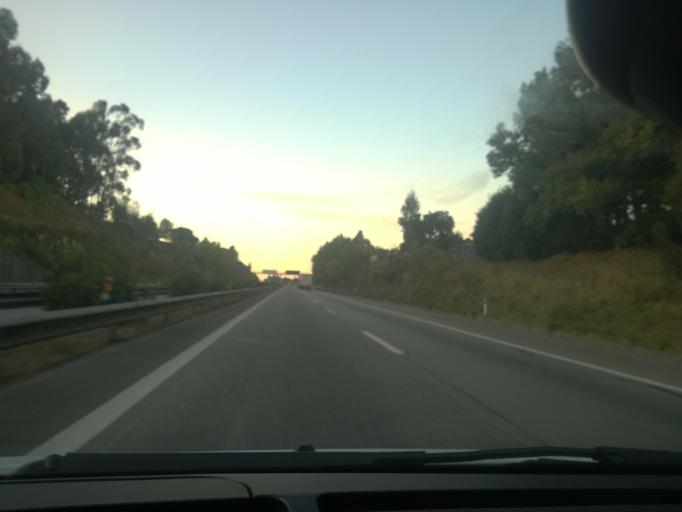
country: PT
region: Porto
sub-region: Vila Nova de Gaia
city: Oliveira do Douro
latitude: 41.1226
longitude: -8.5730
